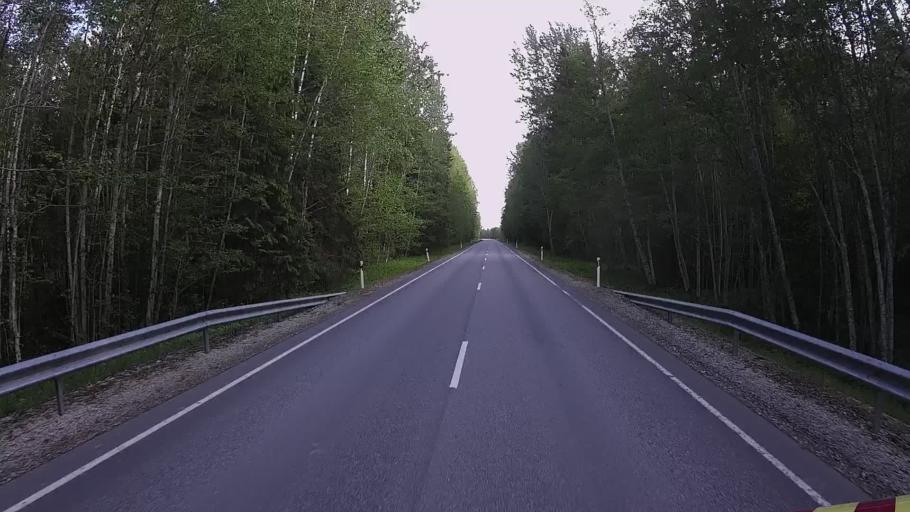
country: EE
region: Jogevamaa
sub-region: Mustvee linn
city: Mustvee
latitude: 58.8848
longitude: 26.8140
